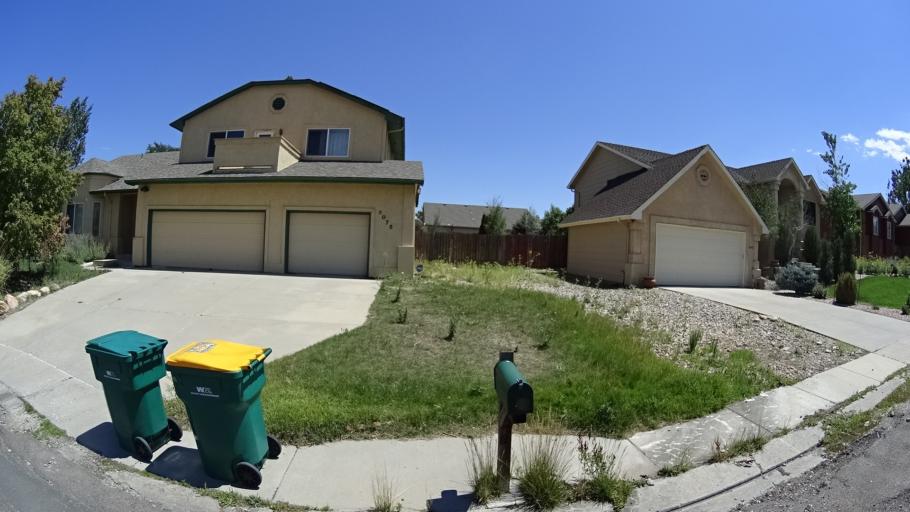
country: US
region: Colorado
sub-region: El Paso County
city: Air Force Academy
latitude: 38.9205
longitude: -104.8379
